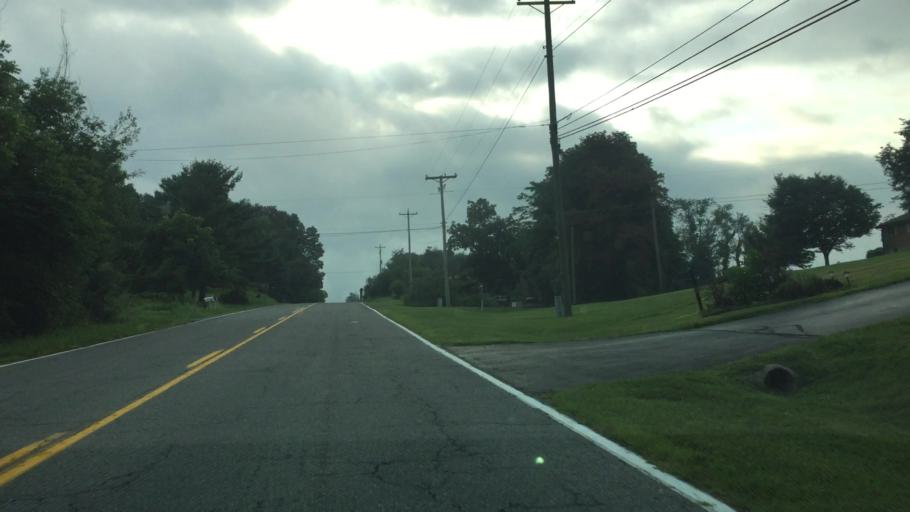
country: US
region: Virginia
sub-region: Pulaski County
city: Pulaski
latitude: 36.9567
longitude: -80.8678
